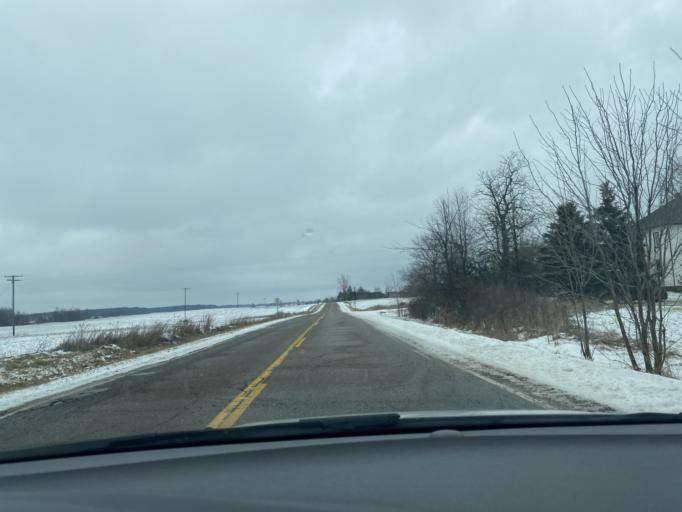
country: US
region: Michigan
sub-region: Lapeer County
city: North Branch
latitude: 43.2093
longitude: -83.1263
